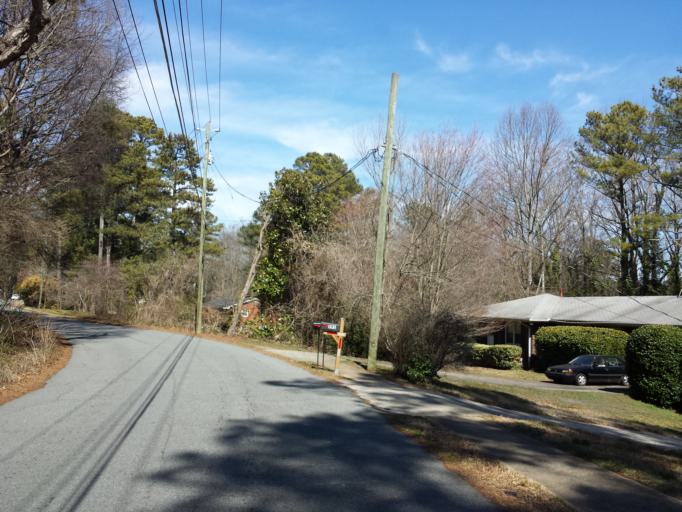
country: US
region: Georgia
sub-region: Cobb County
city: Smyrna
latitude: 33.9374
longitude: -84.4741
